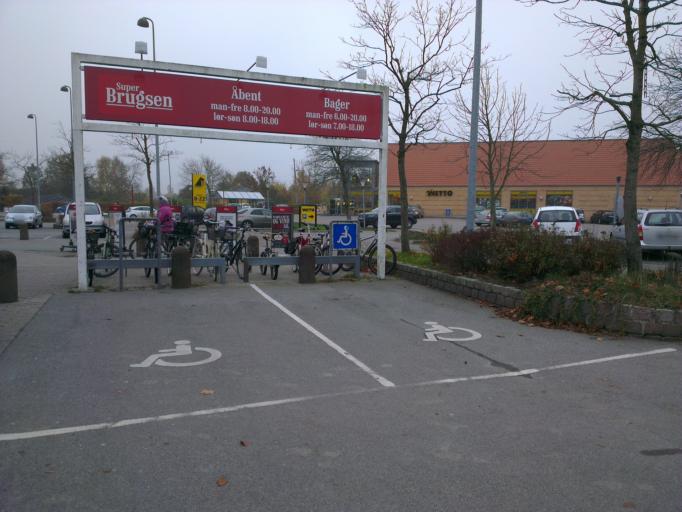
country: DK
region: Capital Region
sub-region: Frederikssund Kommune
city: Slangerup
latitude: 55.8438
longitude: 12.1756
